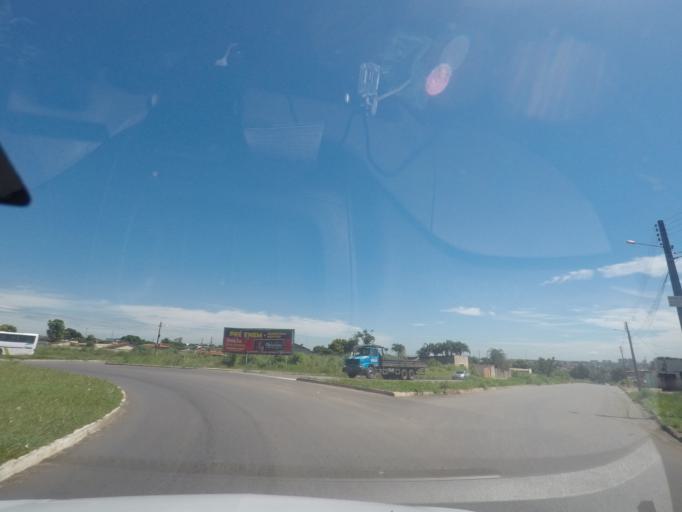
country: BR
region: Goias
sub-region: Aparecida De Goiania
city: Aparecida de Goiania
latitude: -16.7827
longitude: -49.3314
